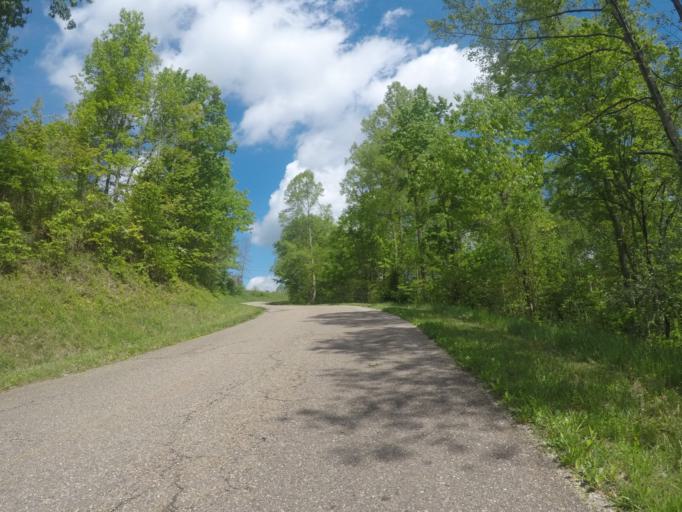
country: US
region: West Virginia
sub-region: Cabell County
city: Huntington
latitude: 38.5418
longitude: -82.4389
